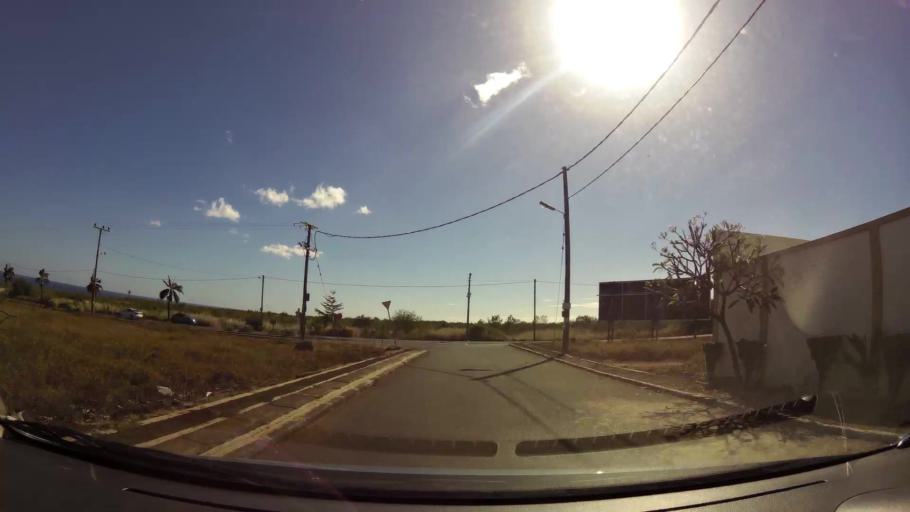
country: MU
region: Black River
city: Flic en Flac
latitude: -20.2770
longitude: 57.3804
